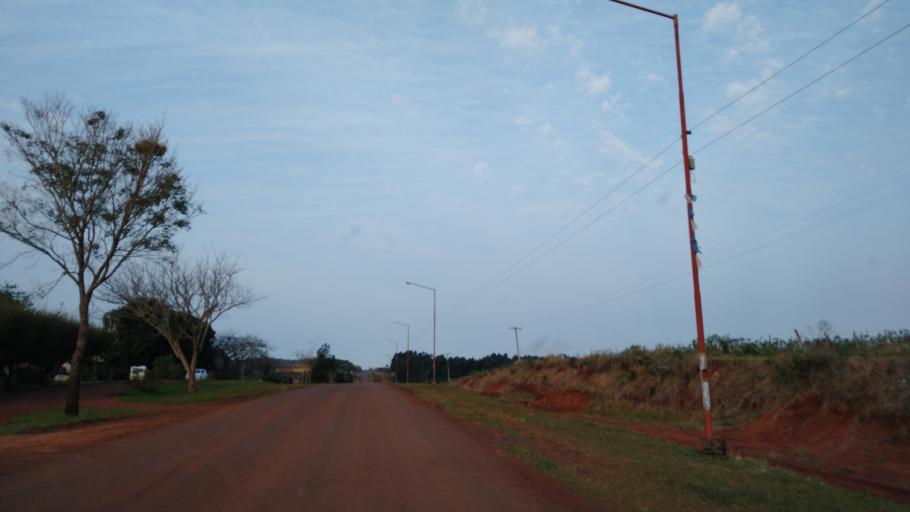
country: AR
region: Corrientes
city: San Carlos
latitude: -27.7519
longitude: -55.8960
